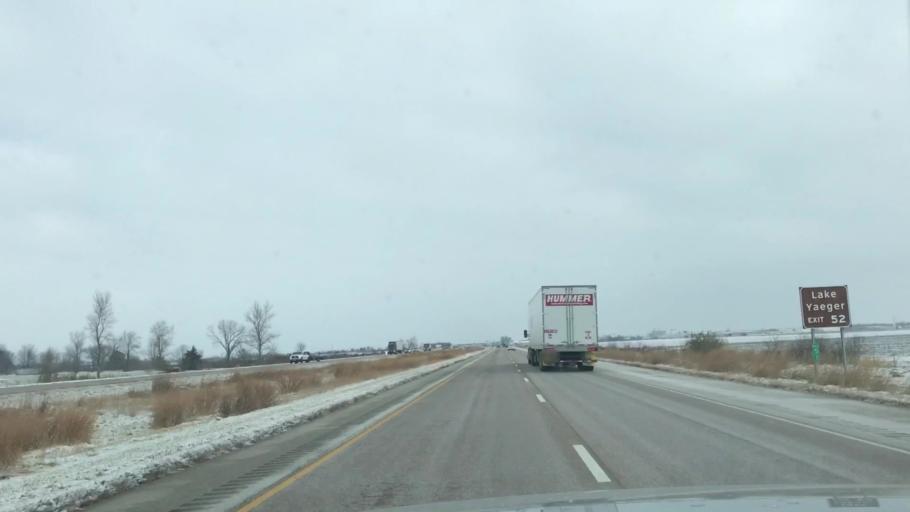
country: US
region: Illinois
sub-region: Montgomery County
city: Litchfield
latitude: 39.1555
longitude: -89.6945
